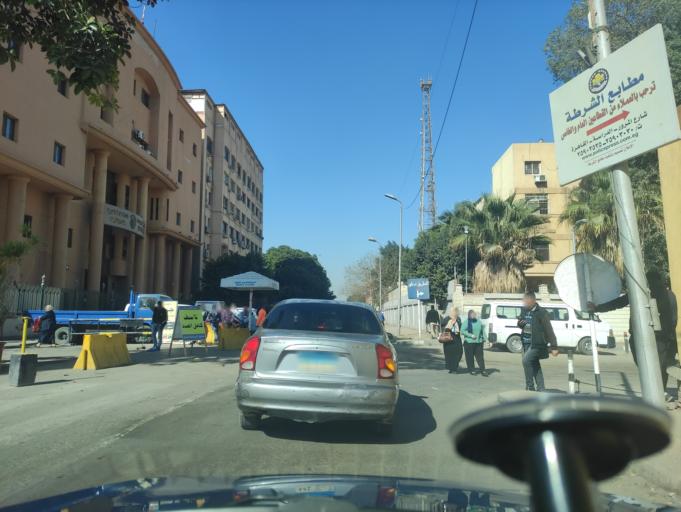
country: EG
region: Muhafazat al Qahirah
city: Cairo
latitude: 30.0524
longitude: 31.2758
